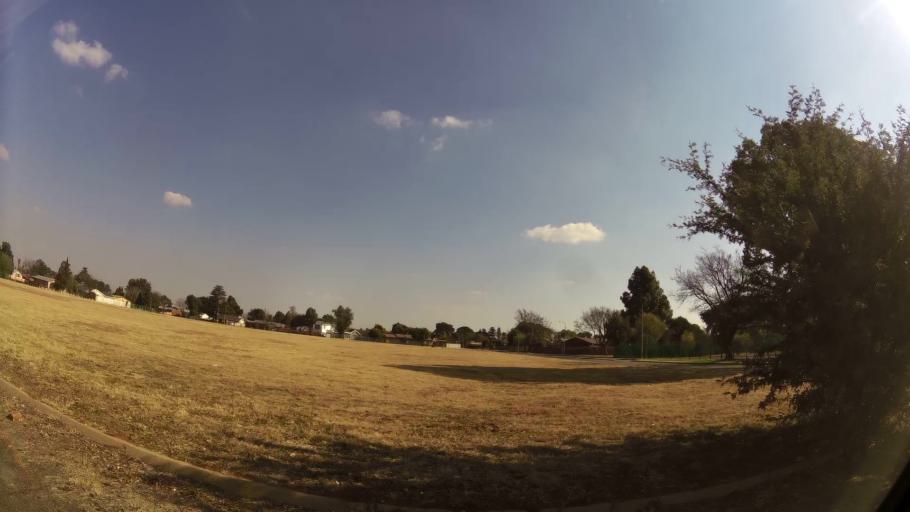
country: ZA
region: Gauteng
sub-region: Ekurhuleni Metropolitan Municipality
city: Boksburg
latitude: -26.2479
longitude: 28.2956
